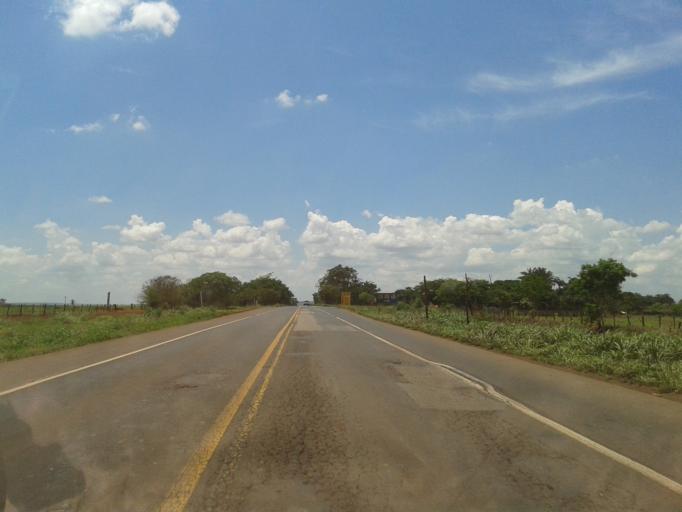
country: BR
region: Goias
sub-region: Goiatuba
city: Goiatuba
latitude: -18.2862
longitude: -49.6105
